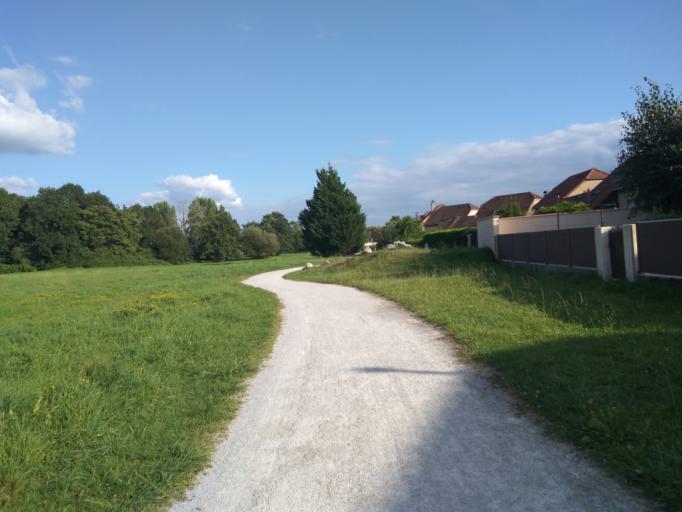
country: FR
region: Aquitaine
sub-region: Departement des Pyrenees-Atlantiques
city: Gelos
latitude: 43.2896
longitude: -0.3752
